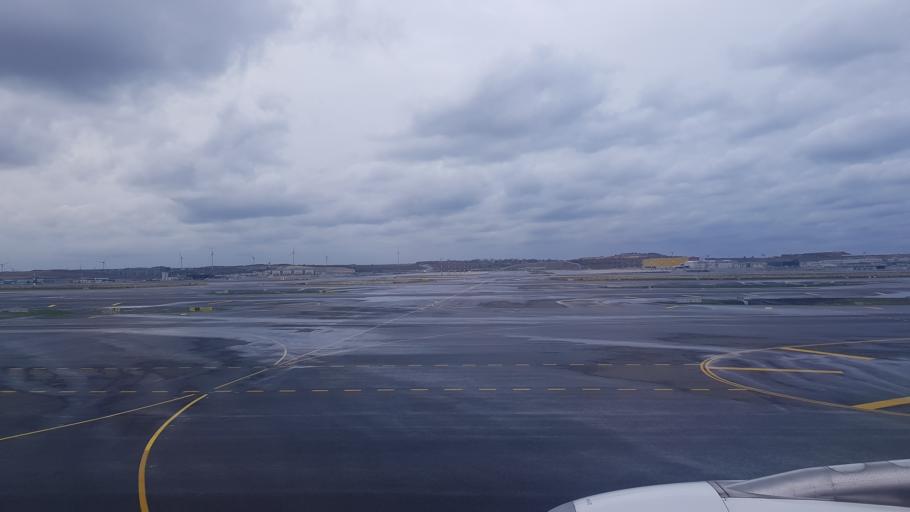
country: TR
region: Istanbul
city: Durusu
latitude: 41.2675
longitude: 28.7334
